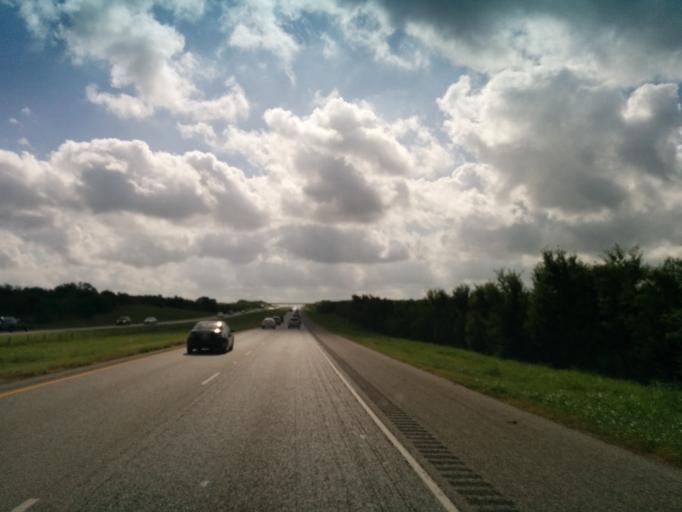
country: US
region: Texas
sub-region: Gonzales County
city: Waelder
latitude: 29.6655
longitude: -97.3465
